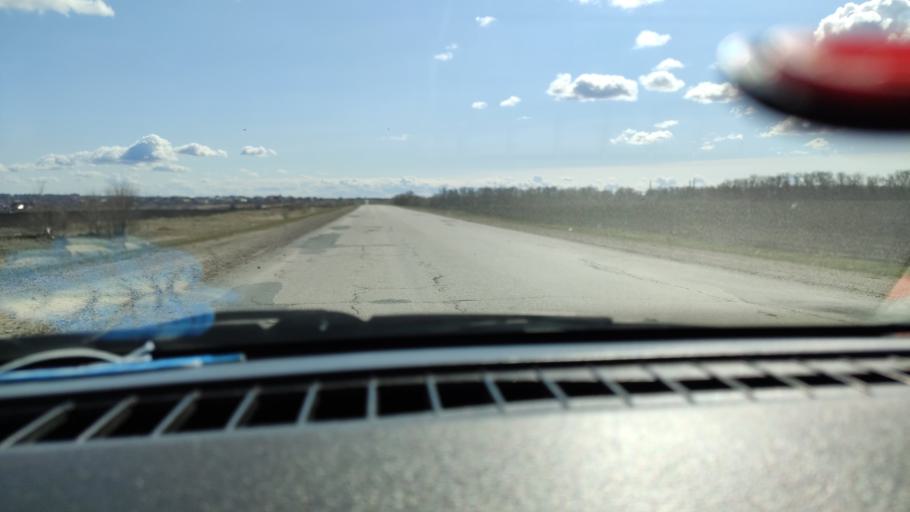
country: RU
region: Samara
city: Varlamovo
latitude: 53.1171
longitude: 48.3425
